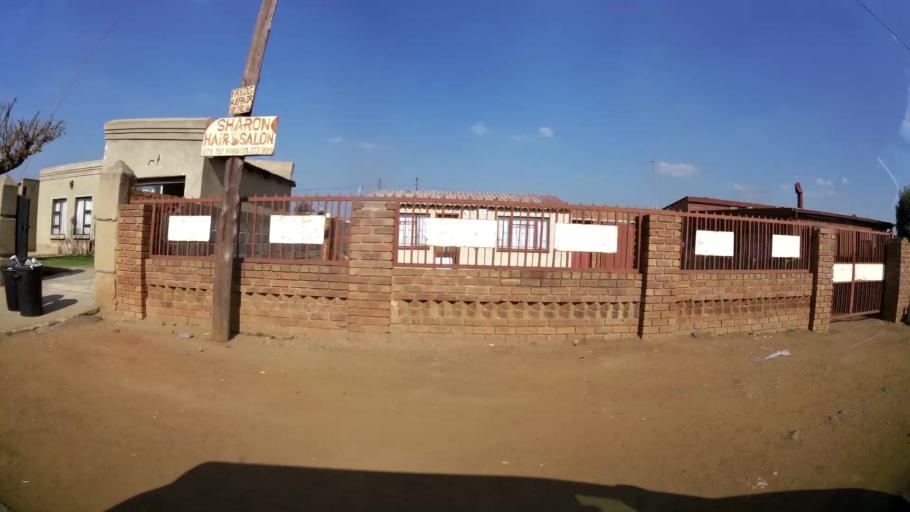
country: ZA
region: Gauteng
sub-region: Ekurhuleni Metropolitan Municipality
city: Brakpan
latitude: -26.1570
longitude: 28.4065
